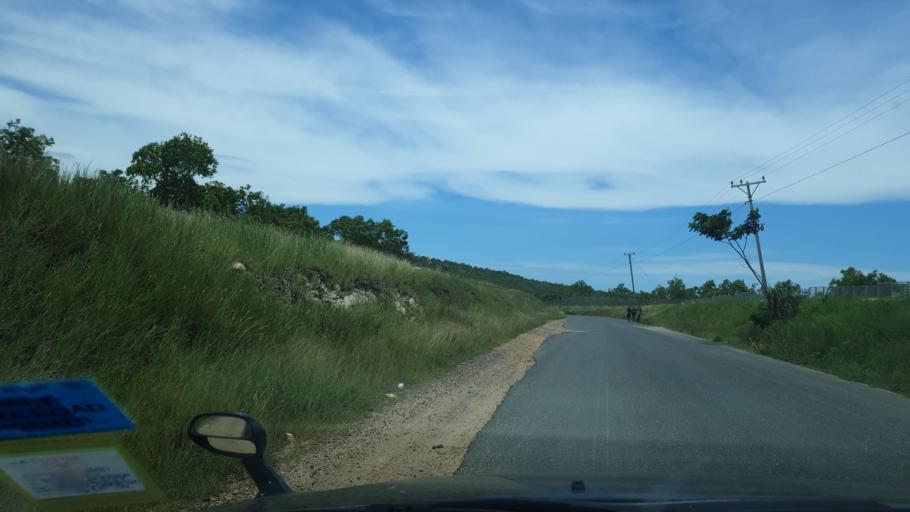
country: PG
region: National Capital
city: Port Moresby
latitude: -9.4409
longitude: 147.0756
